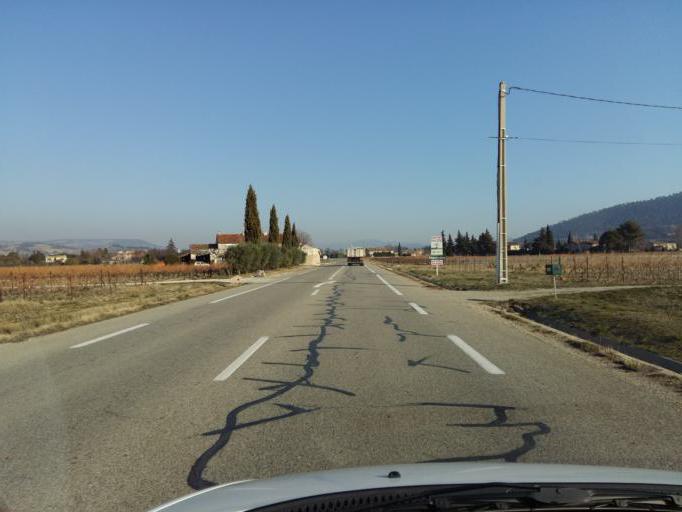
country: FR
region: Provence-Alpes-Cote d'Azur
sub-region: Departement du Vaucluse
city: Sablet
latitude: 44.2155
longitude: 5.0059
